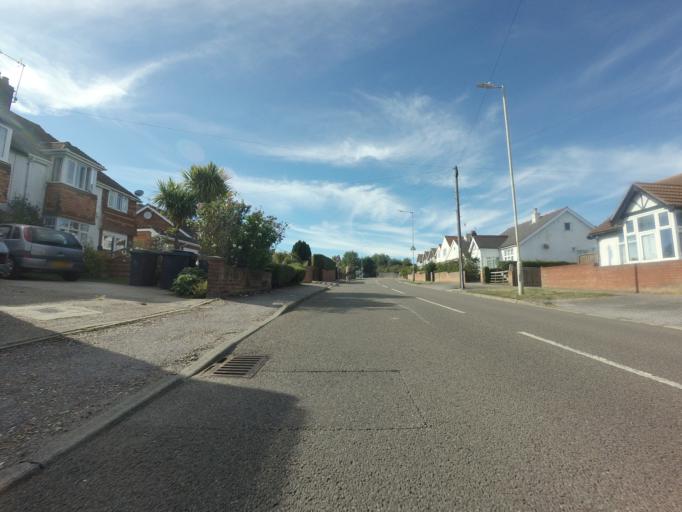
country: GB
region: England
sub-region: Kent
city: Herne Bay
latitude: 51.3713
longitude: 1.1608
